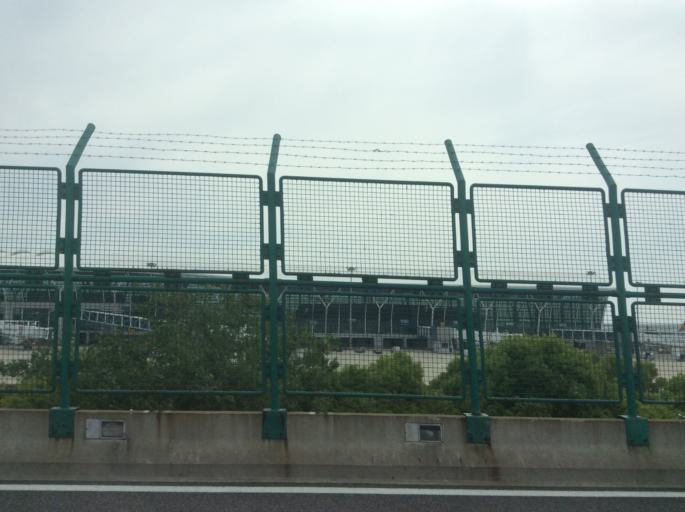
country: CN
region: Shanghai Shi
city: Laogang
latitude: 31.1476
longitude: 121.8058
